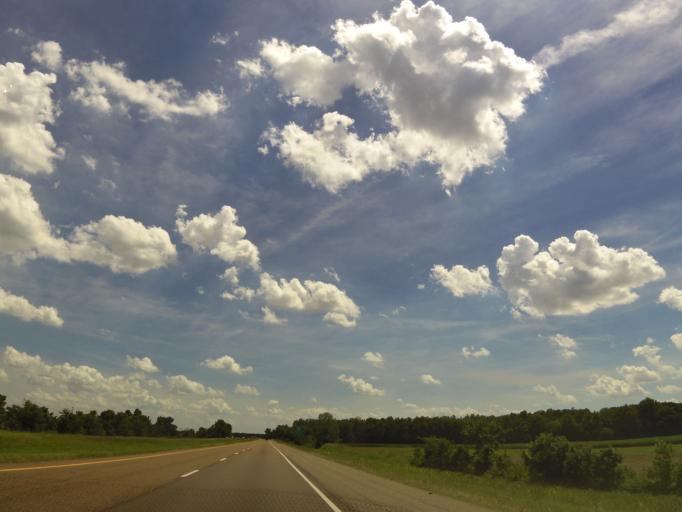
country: US
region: Tennessee
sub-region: Dyer County
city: Dyersburg
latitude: 36.0408
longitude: -89.3376
